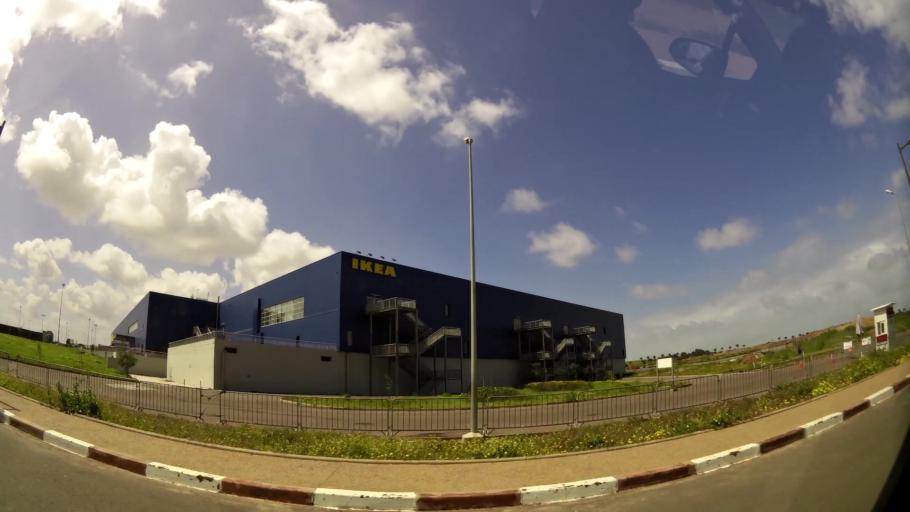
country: MA
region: Grand Casablanca
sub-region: Mediouna
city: Tit Mellil
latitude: 33.6310
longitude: -7.4583
